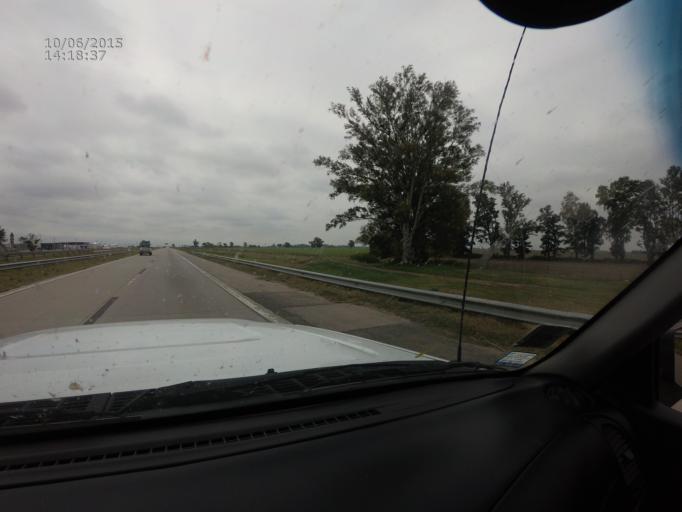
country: AR
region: Cordoba
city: Villa Maria
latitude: -32.3685
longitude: -63.2242
